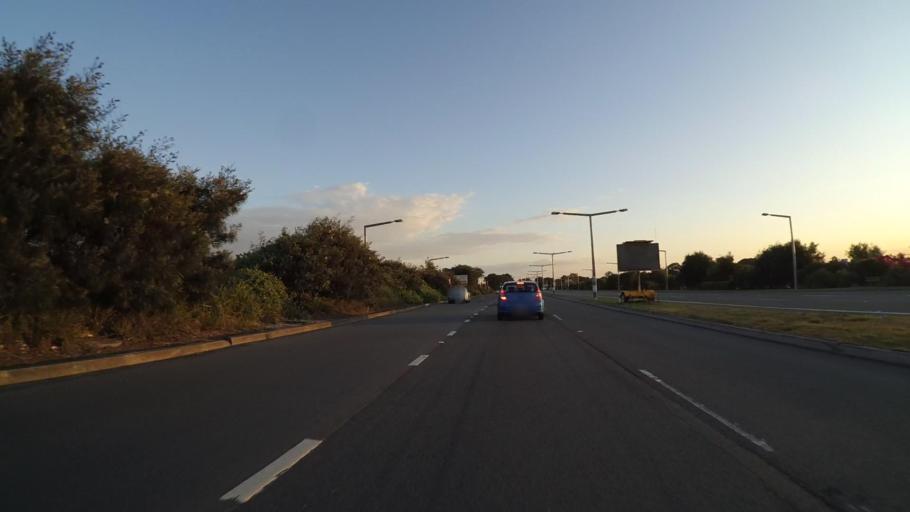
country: AU
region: New South Wales
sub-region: Botany Bay
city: Mascot
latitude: -33.9361
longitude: 151.1929
